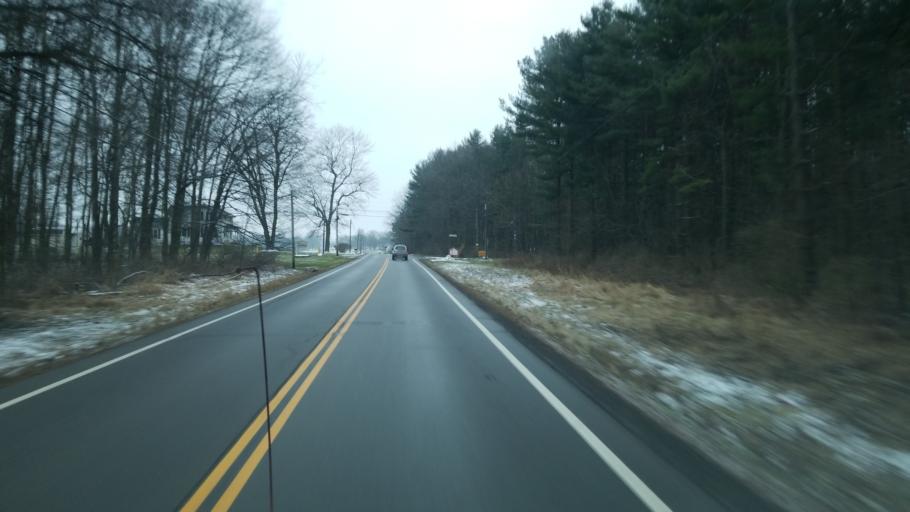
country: US
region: Ohio
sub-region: Wayne County
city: Shreve
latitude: 40.7666
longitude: -82.0489
